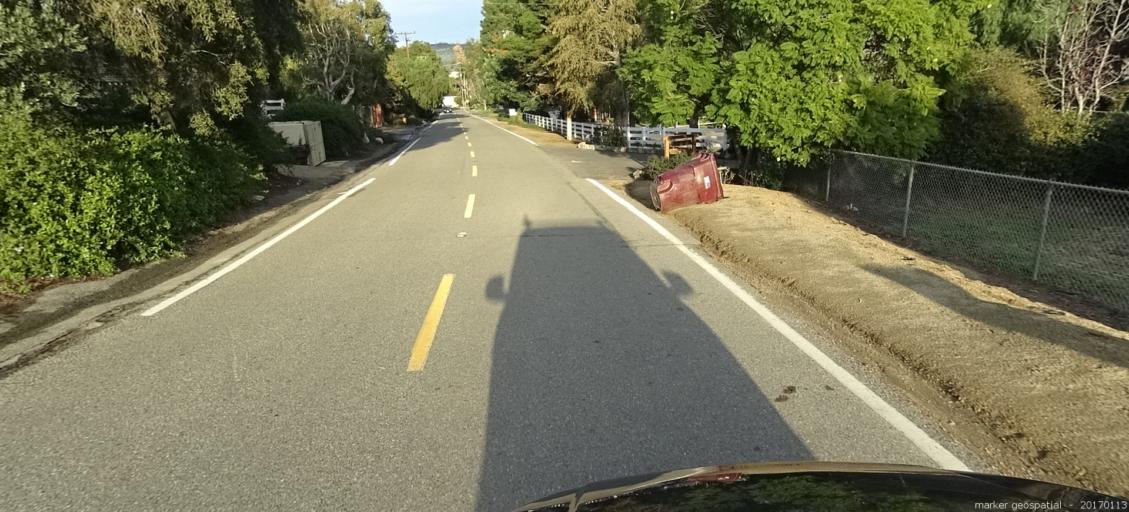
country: US
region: California
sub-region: Orange County
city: Villa Park
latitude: 33.8036
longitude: -117.7866
